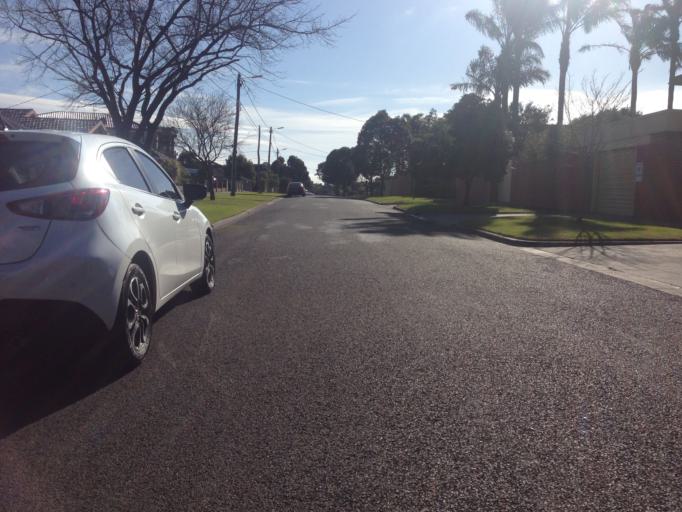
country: AU
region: Victoria
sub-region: Darebin
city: Preston
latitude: -37.7644
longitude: 145.0195
